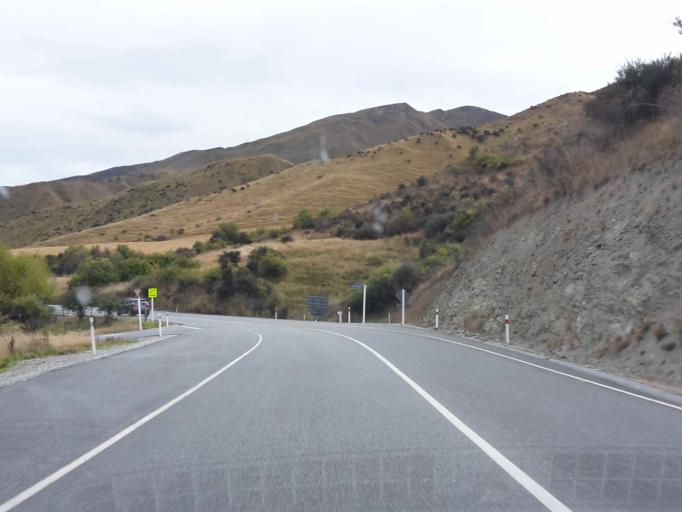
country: NZ
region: Otago
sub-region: Queenstown-Lakes District
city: Arrowtown
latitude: -44.9862
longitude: 168.9030
